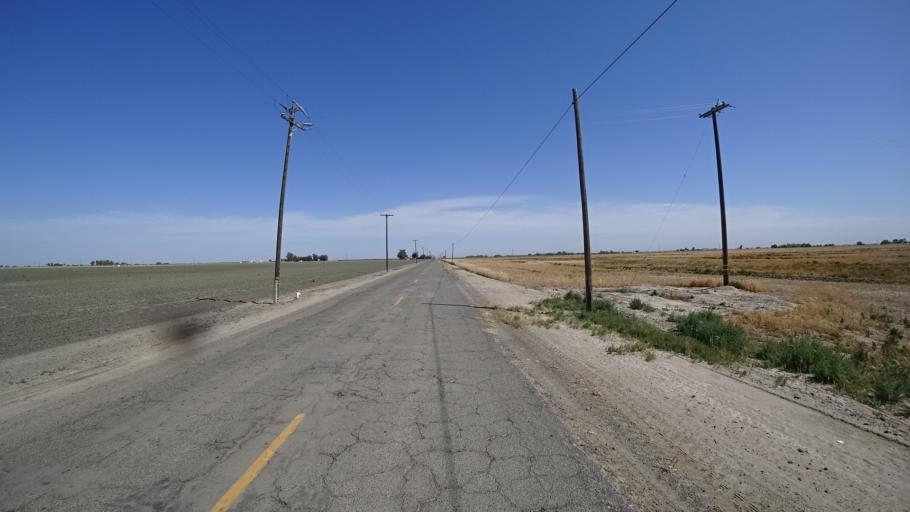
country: US
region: California
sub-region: Kings County
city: Stratford
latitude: 36.1927
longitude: -119.8340
